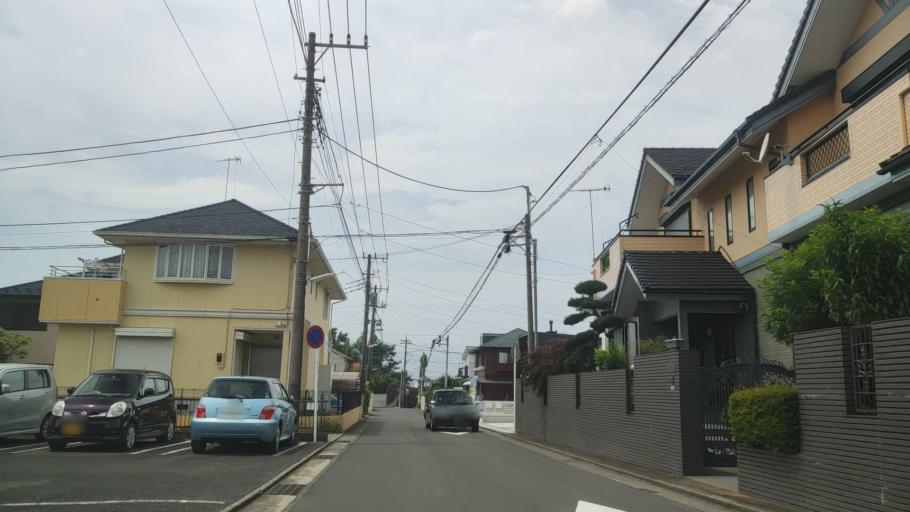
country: JP
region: Kanagawa
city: Atsugi
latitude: 35.4337
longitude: 139.3946
